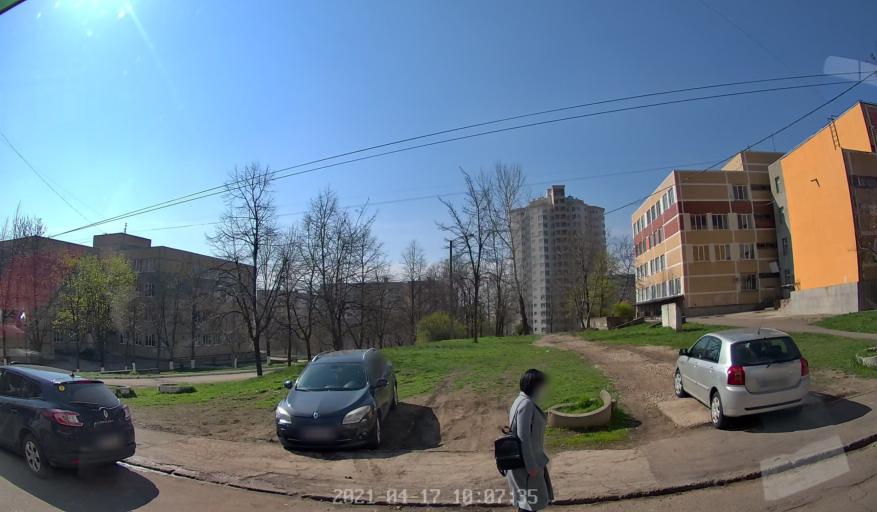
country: MD
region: Chisinau
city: Chisinau
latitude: 47.0417
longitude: 28.8941
